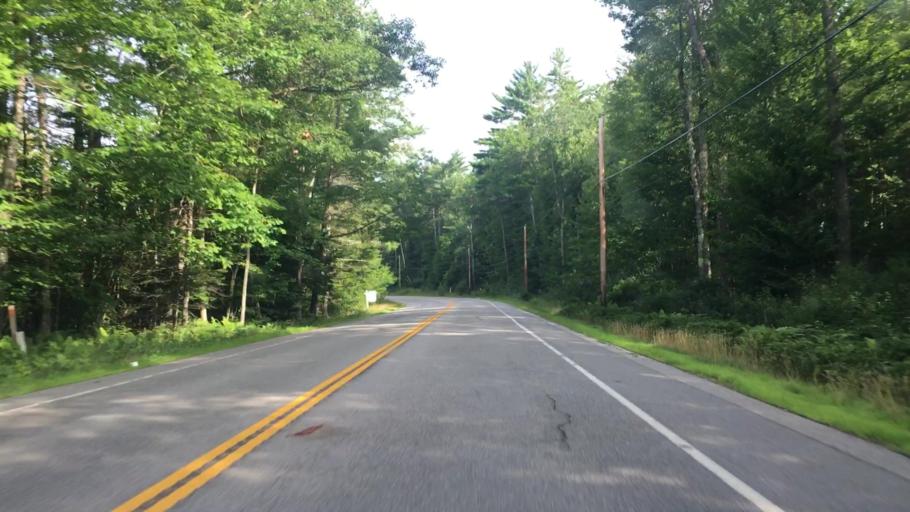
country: US
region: Maine
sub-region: York County
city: Limington
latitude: 43.7643
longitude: -70.7115
